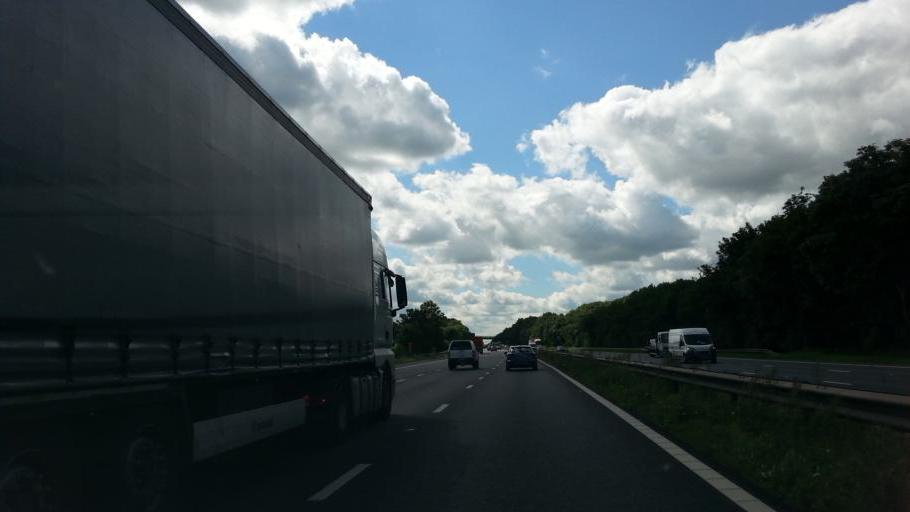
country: GB
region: England
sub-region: Leicestershire
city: Lutterworth
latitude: 52.4907
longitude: -1.1917
